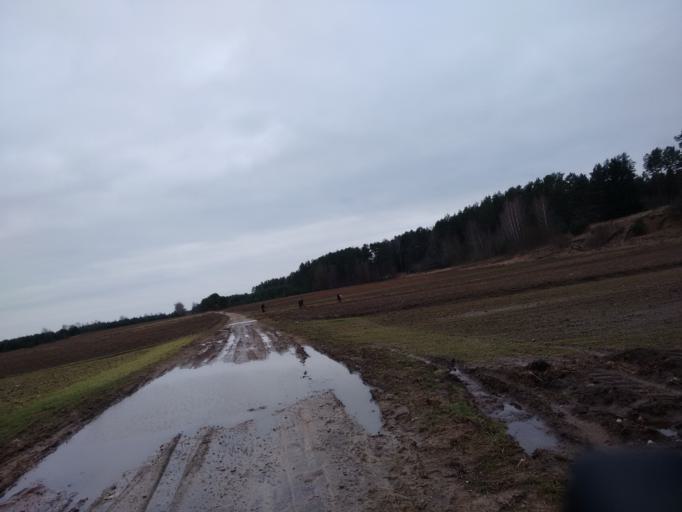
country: LT
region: Alytaus apskritis
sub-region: Alytus
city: Alytus
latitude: 54.2277
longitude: 23.9586
